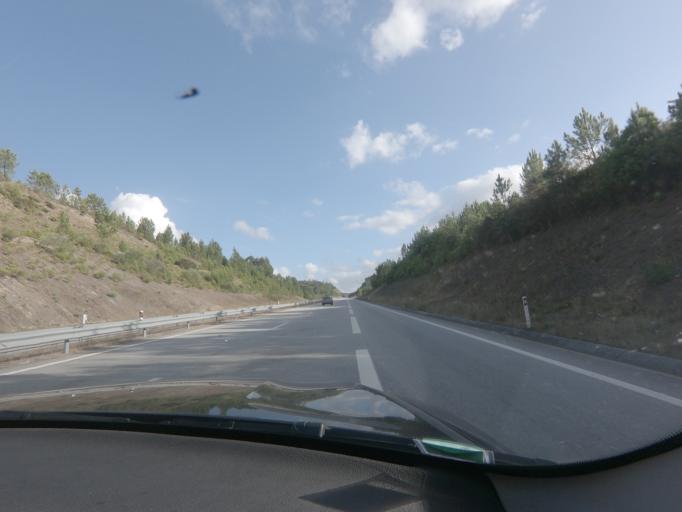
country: PT
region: Viseu
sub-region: Viseu
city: Campo
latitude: 40.7896
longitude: -7.9287
